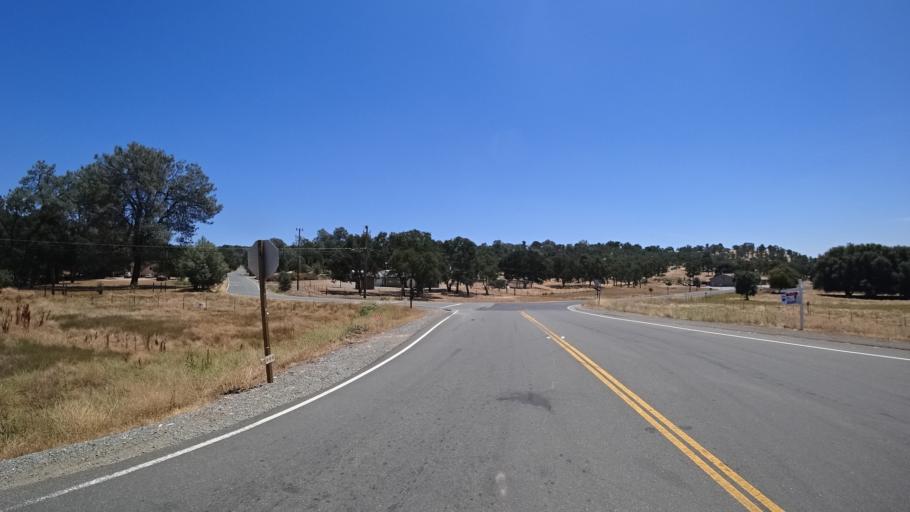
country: US
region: California
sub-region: Calaveras County
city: Rancho Calaveras
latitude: 38.1225
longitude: -120.8774
